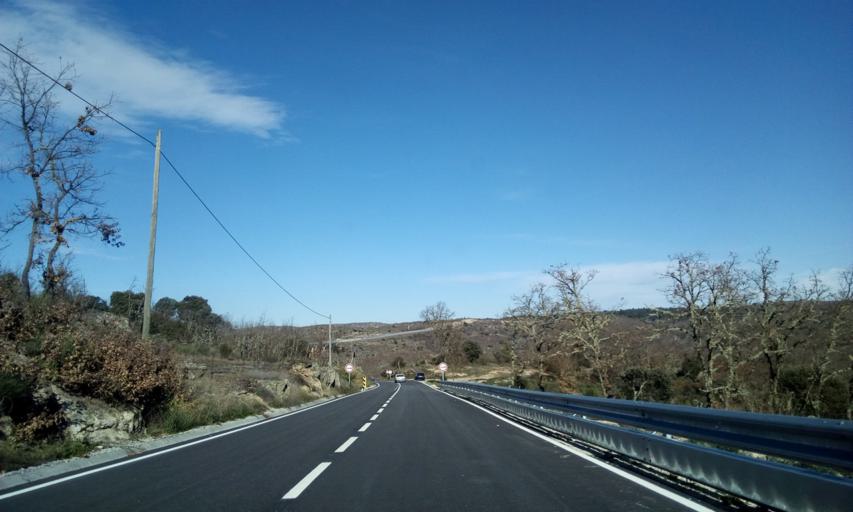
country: ES
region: Castille and Leon
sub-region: Provincia de Salamanca
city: Fuentes de Onoro
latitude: 40.6044
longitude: -6.9269
